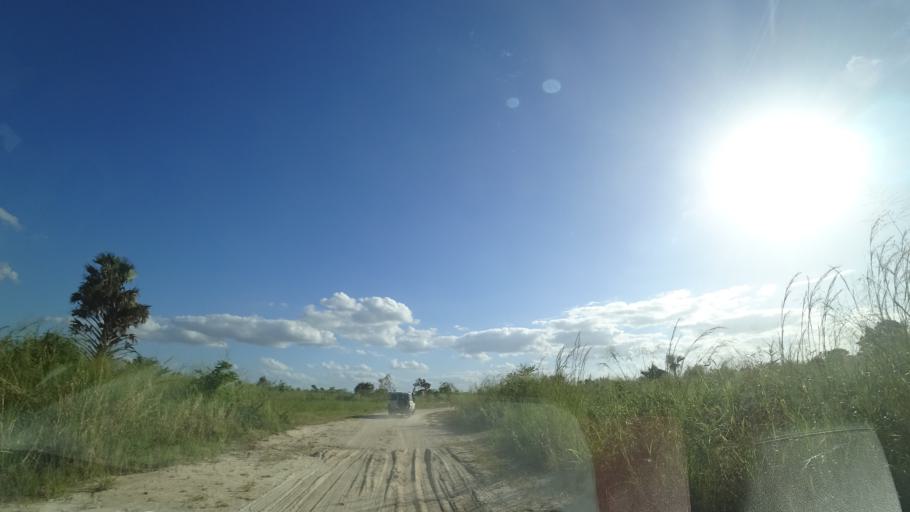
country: MZ
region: Sofala
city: Dondo
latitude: -19.3867
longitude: 34.5917
